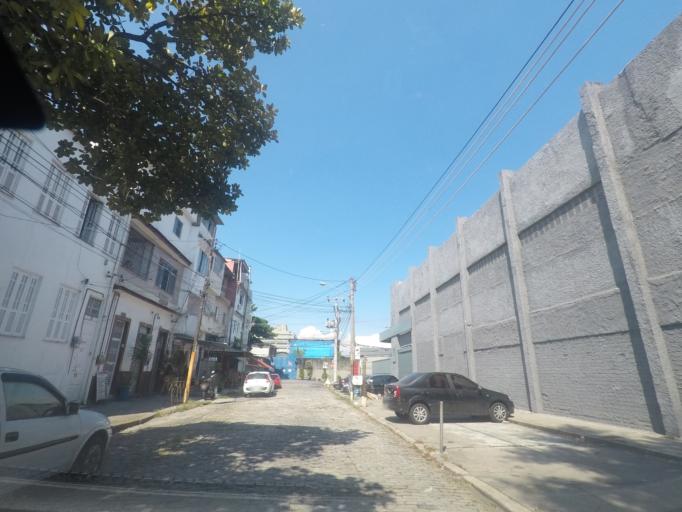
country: BR
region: Rio de Janeiro
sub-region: Rio De Janeiro
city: Rio de Janeiro
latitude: -22.8961
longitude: -43.2180
